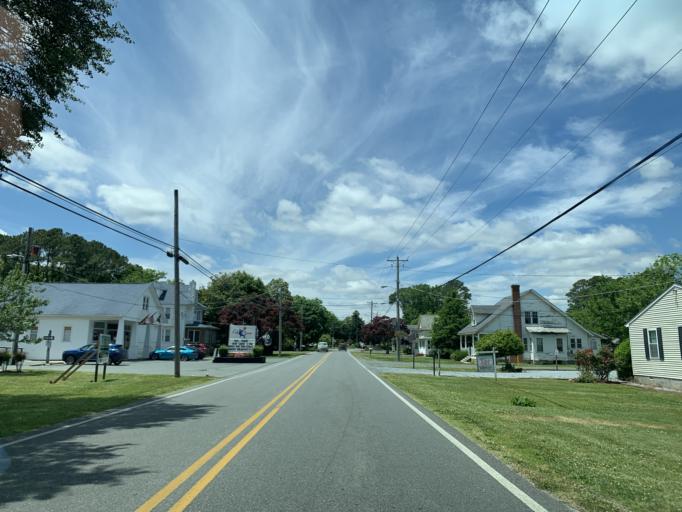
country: US
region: Maryland
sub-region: Worcester County
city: West Ocean City
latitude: 38.3324
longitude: -75.1110
